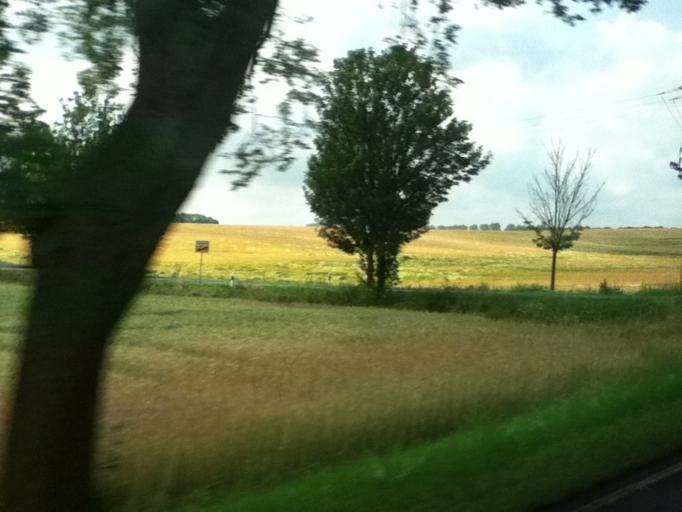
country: DE
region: Thuringia
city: Frankendorf
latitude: 50.9668
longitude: 11.4515
